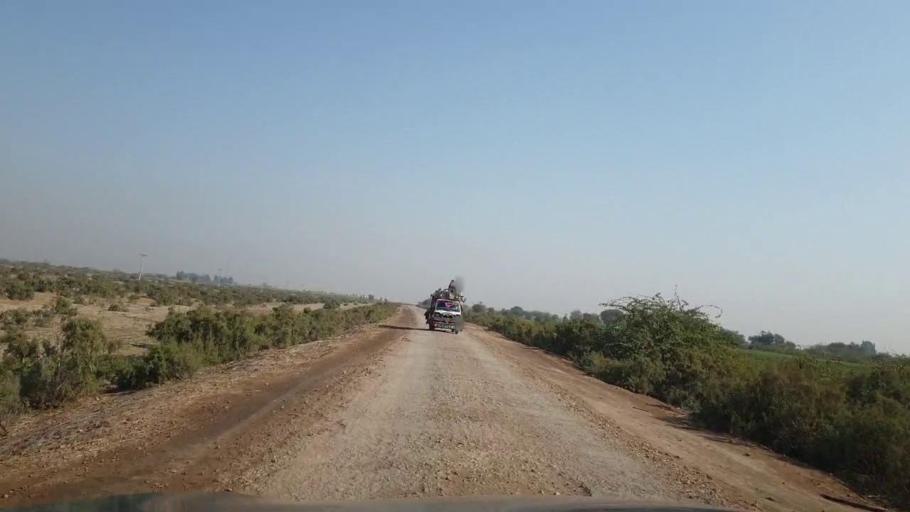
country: PK
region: Sindh
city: Berani
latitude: 25.6321
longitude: 68.8635
